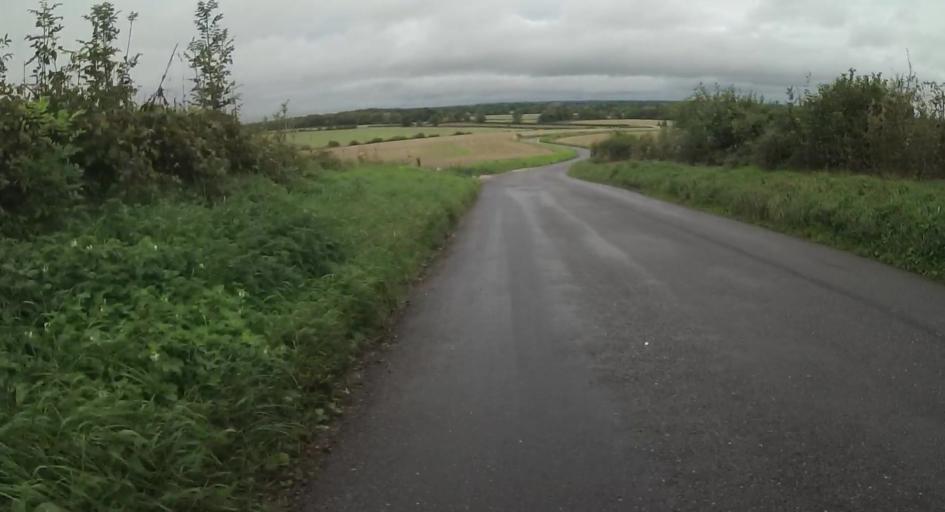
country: GB
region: England
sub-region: Hampshire
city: Tadley
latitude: 51.2958
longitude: -1.1516
